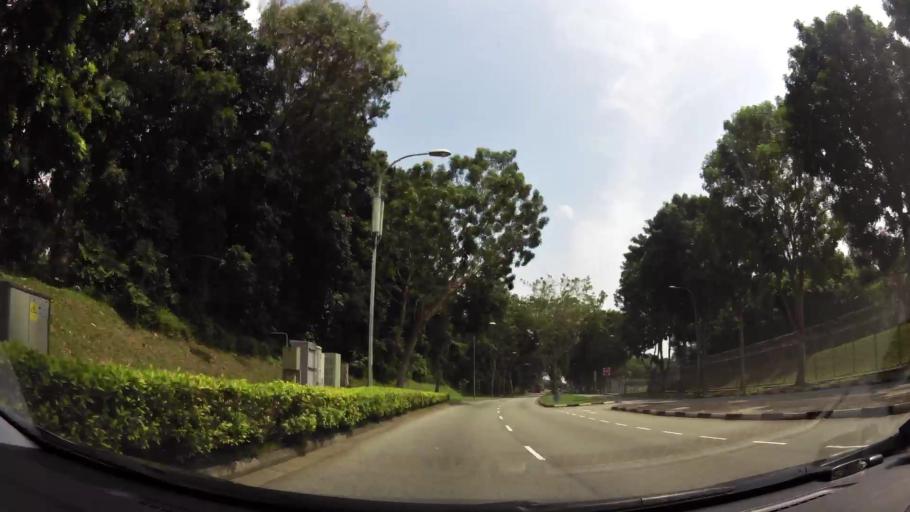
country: MY
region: Johor
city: Kampung Pasir Gudang Baru
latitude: 1.3880
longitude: 103.9824
